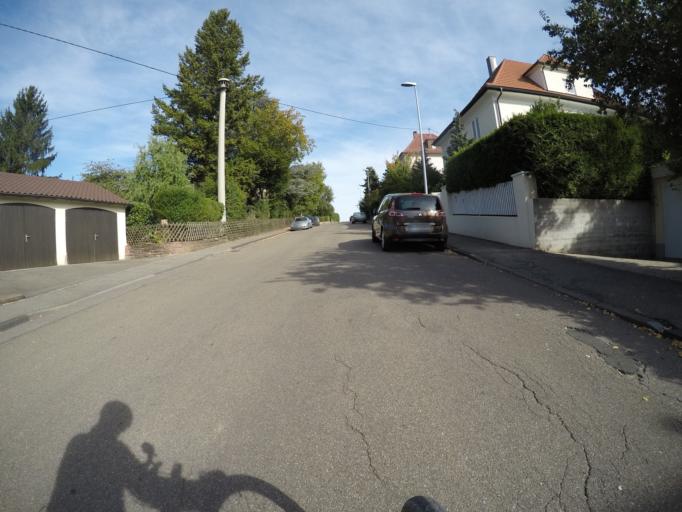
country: DE
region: Baden-Wuerttemberg
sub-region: Regierungsbezirk Stuttgart
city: Korntal
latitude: 48.8346
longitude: 9.1149
